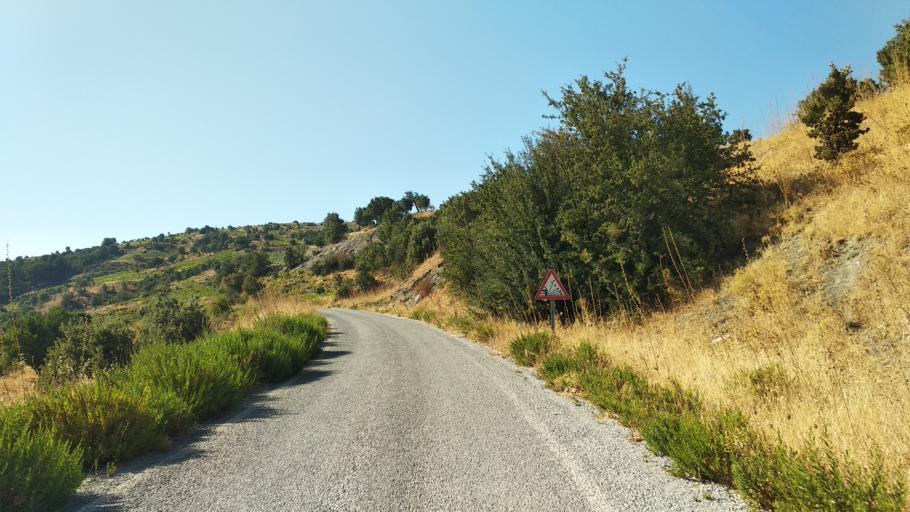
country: TR
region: Izmir
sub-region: Seferihisar
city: Seferhisar
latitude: 38.3280
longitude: 26.9503
